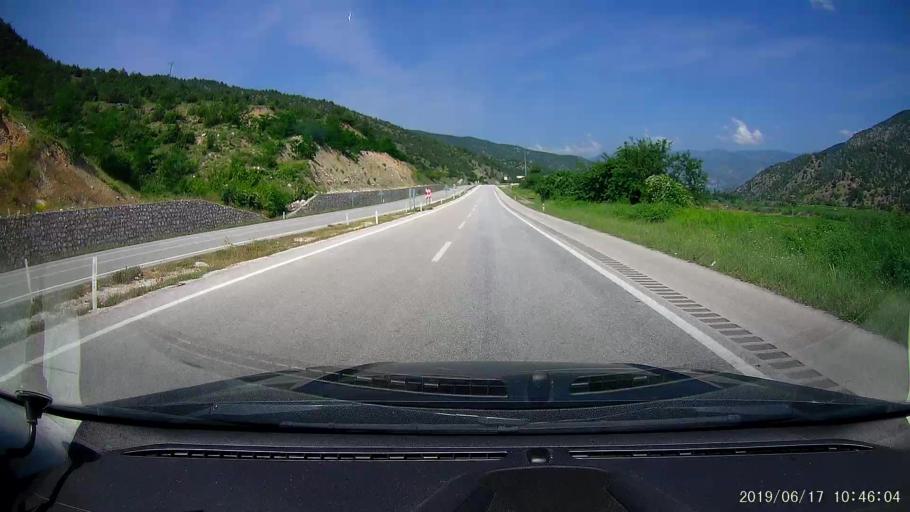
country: TR
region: Corum
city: Hacihamza
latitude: 41.0645
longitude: 34.4715
